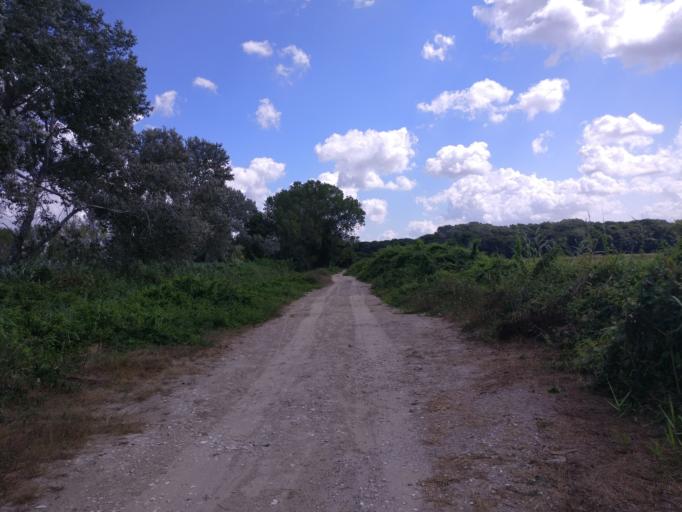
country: IT
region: Tuscany
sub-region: Province of Pisa
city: Marina di Pisa-Tirrenia-Calambrone
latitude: 43.6204
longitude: 10.3093
